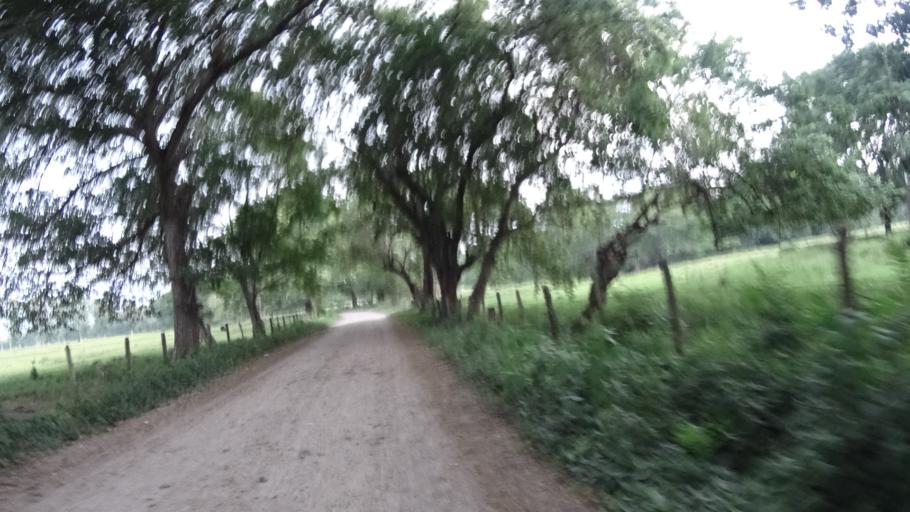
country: CO
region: Cundinamarca
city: Puerto Salgar
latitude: 5.4818
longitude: -74.6878
